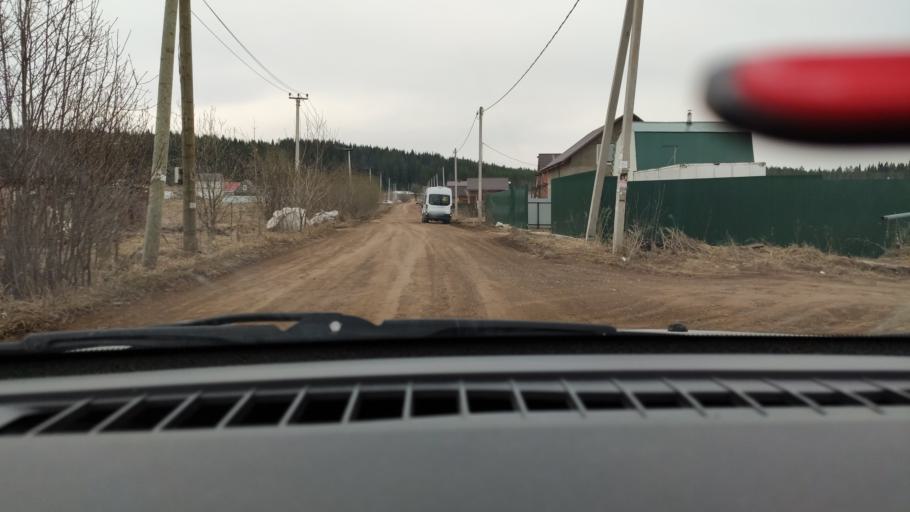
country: RU
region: Perm
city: Kultayevo
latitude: 57.8964
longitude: 56.0154
